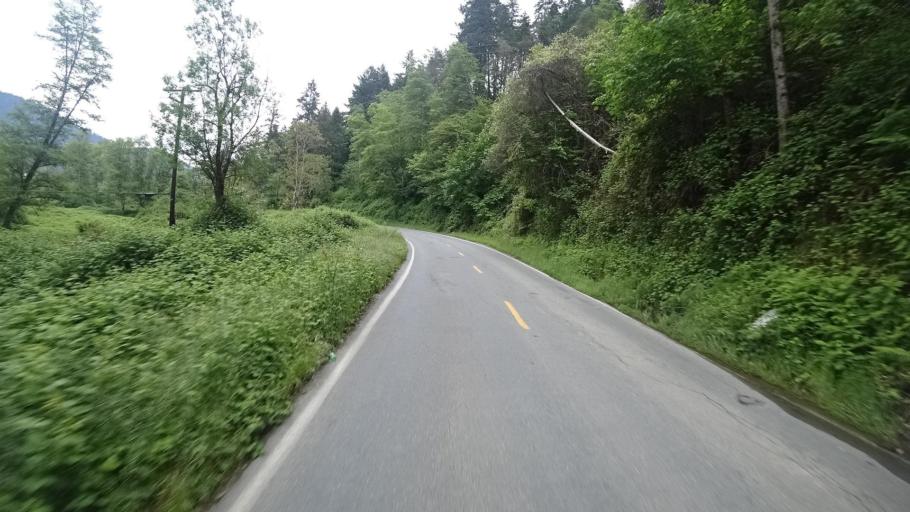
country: US
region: California
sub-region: Humboldt County
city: Willow Creek
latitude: 41.0597
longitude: -123.6921
